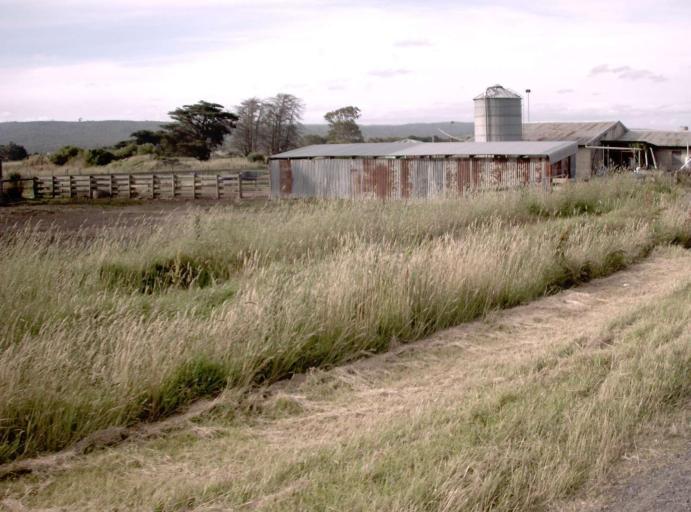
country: AU
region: Victoria
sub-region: Latrobe
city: Traralgon
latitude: -38.0972
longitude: 146.5967
